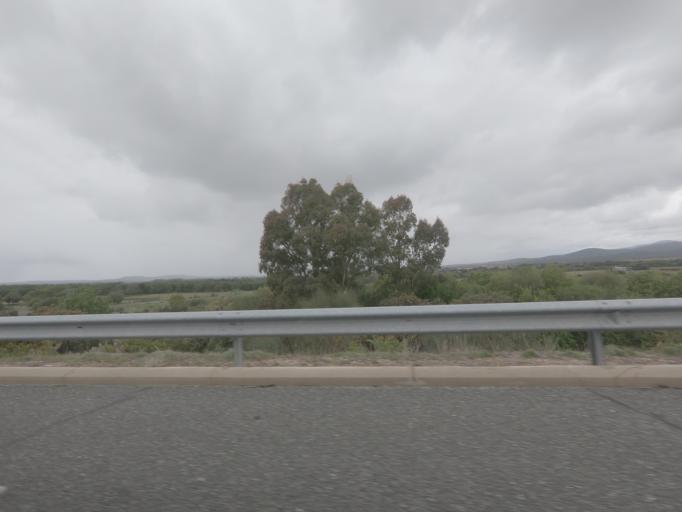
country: ES
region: Extremadura
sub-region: Provincia de Caceres
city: Casas del Monte
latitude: 40.2280
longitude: -5.9780
